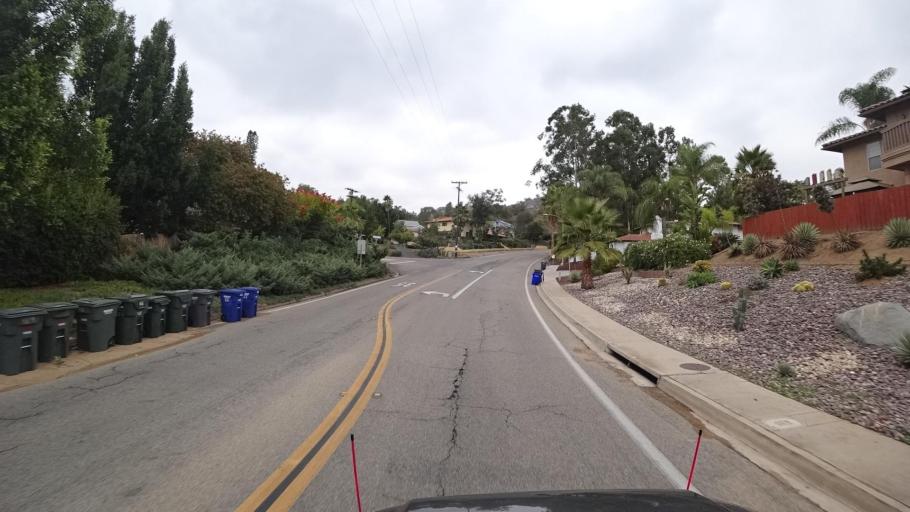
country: US
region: California
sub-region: San Diego County
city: Spring Valley
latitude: 32.7566
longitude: -116.9872
